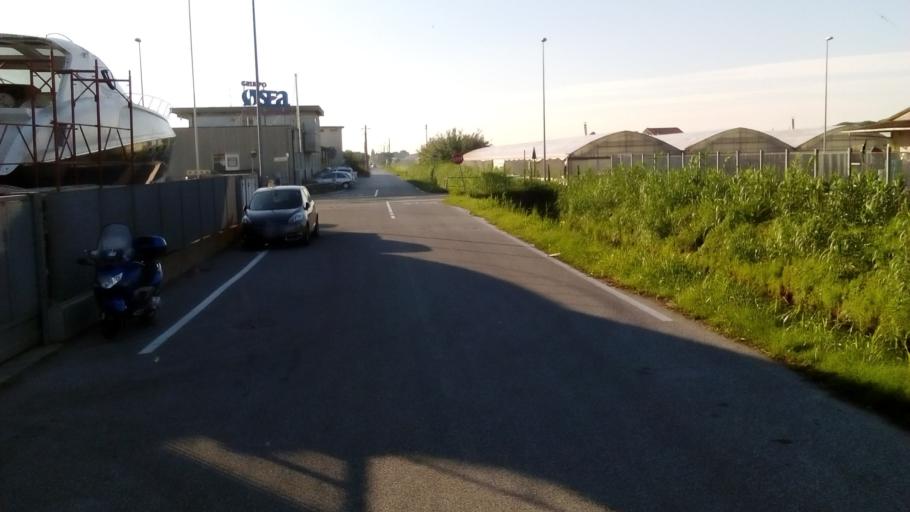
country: IT
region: Tuscany
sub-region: Provincia di Lucca
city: Viareggio
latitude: 43.8580
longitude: 10.2769
